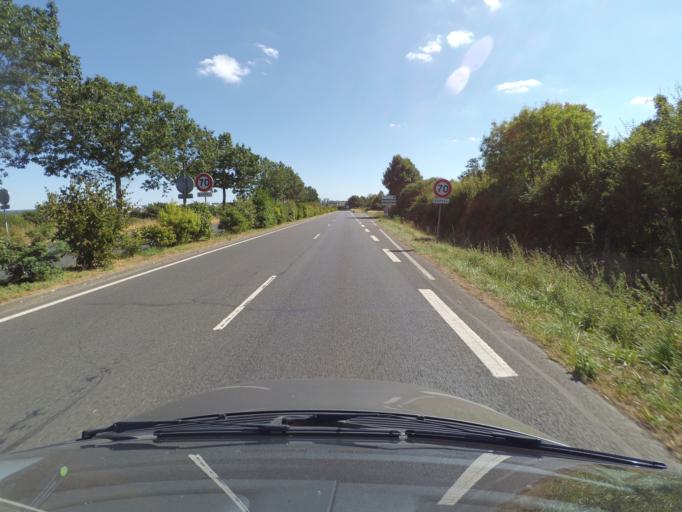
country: FR
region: Pays de la Loire
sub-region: Departement de Maine-et-Loire
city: Cholet
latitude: 47.0636
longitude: -0.9055
